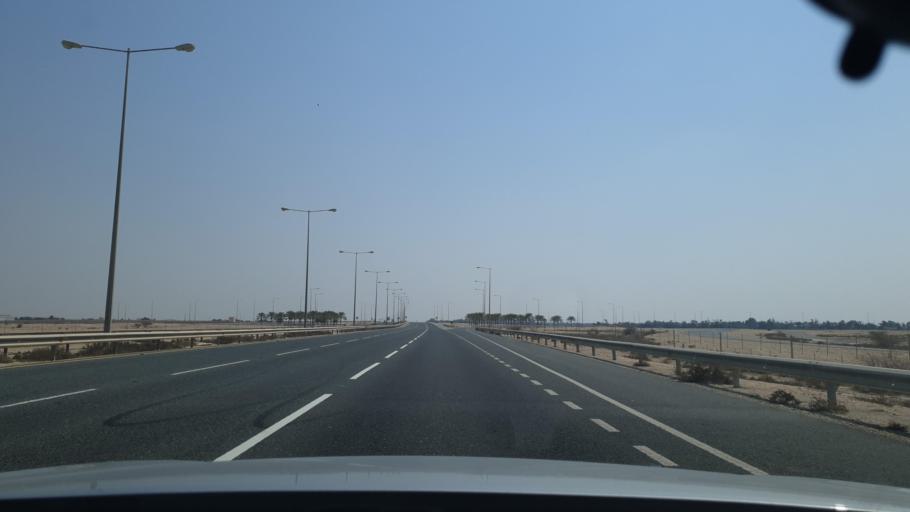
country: QA
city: Al Ghuwayriyah
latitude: 25.7900
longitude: 51.3920
